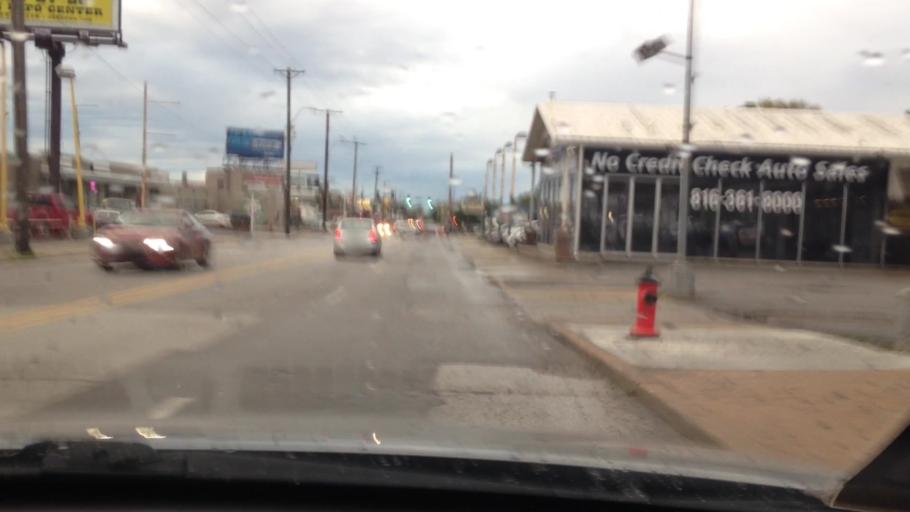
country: US
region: Kansas
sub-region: Johnson County
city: Leawood
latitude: 38.9867
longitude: -94.5945
